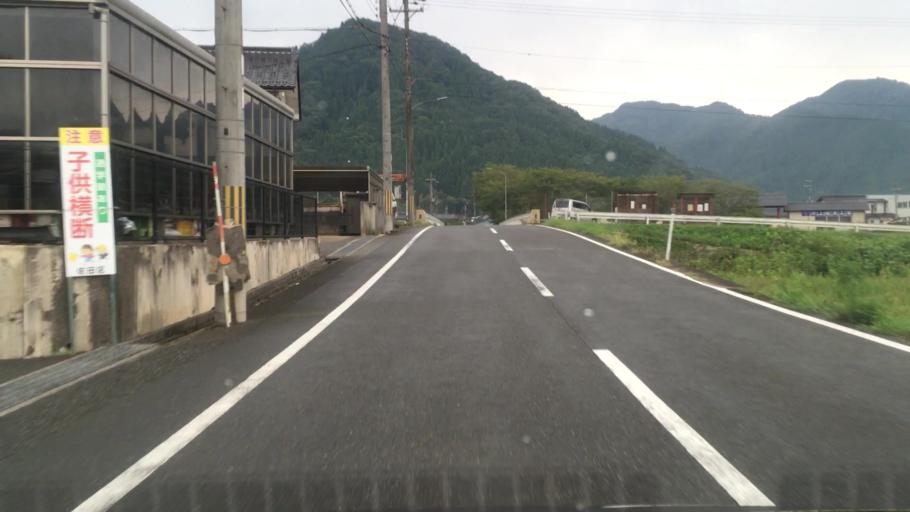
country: JP
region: Hyogo
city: Toyooka
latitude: 35.4572
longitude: 134.7354
